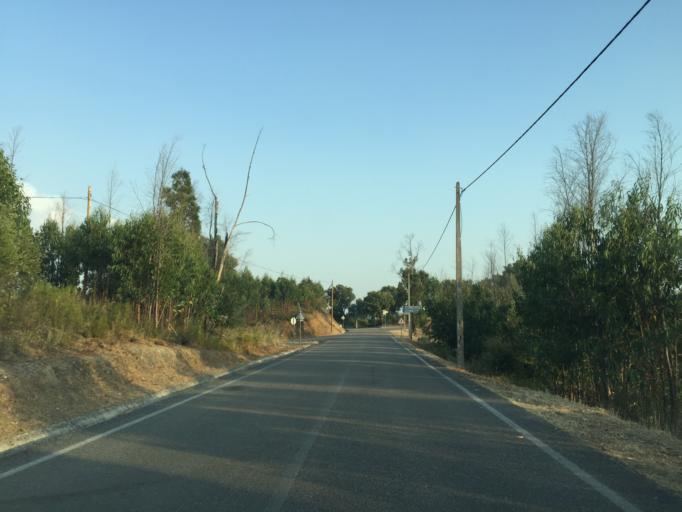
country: PT
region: Santarem
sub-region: Tomar
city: Tomar
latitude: 39.5793
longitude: -8.2976
